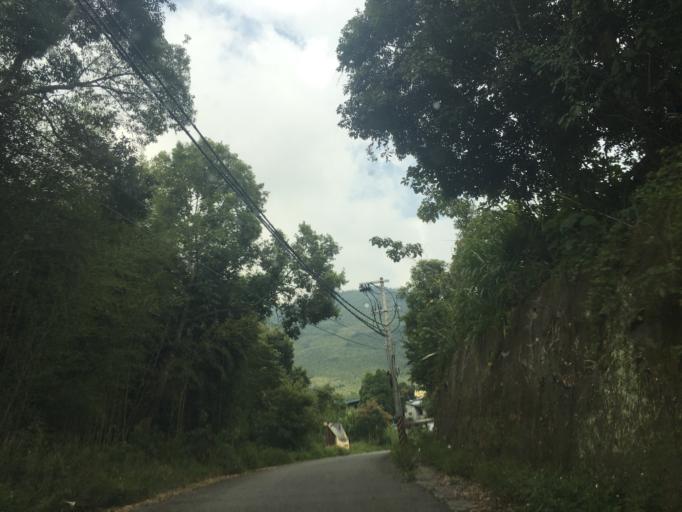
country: TW
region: Taiwan
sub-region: Miaoli
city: Miaoli
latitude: 24.3916
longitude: 120.9755
